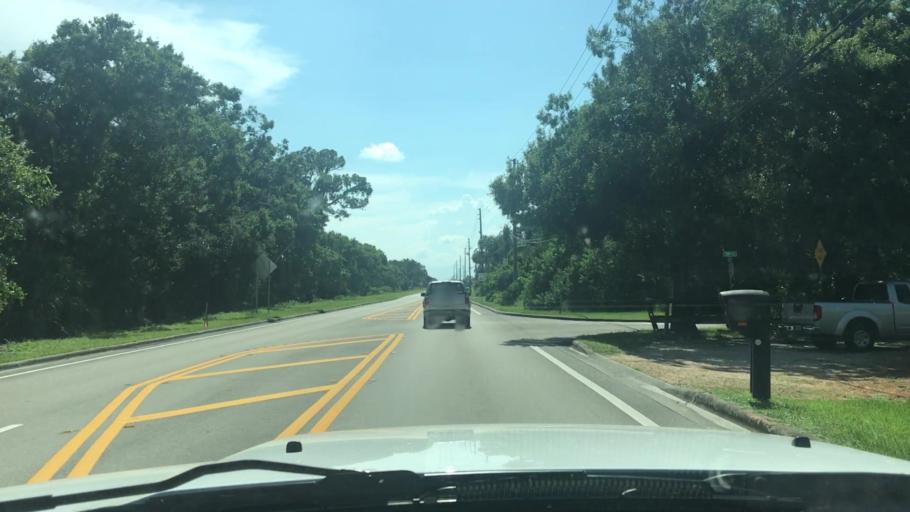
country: US
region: Florida
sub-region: Indian River County
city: West Vero Corridor
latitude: 27.6462
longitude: -80.4478
